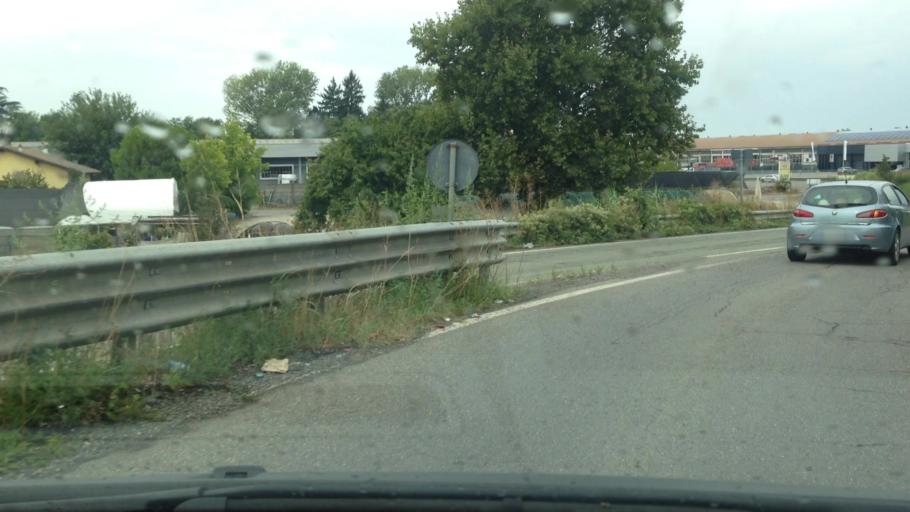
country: IT
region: Piedmont
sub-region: Provincia di Alessandria
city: Tortona
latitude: 44.8936
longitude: 8.8388
